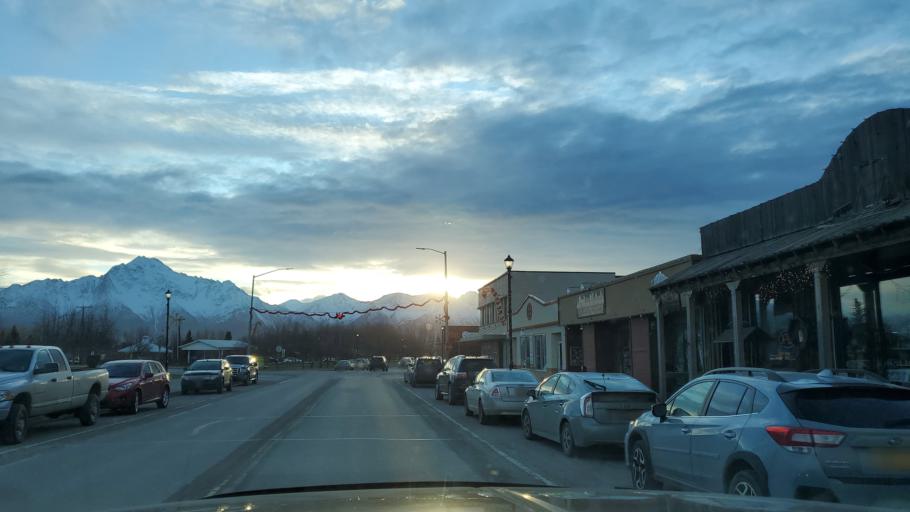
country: US
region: Alaska
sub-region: Matanuska-Susitna Borough
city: Palmer
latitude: 61.6001
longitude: -149.1146
